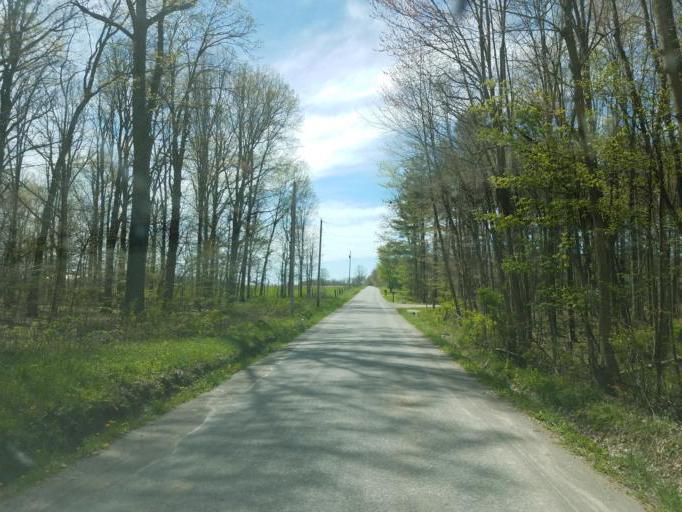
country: US
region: Ohio
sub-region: Ashland County
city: Ashland
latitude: 40.9020
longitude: -82.3959
